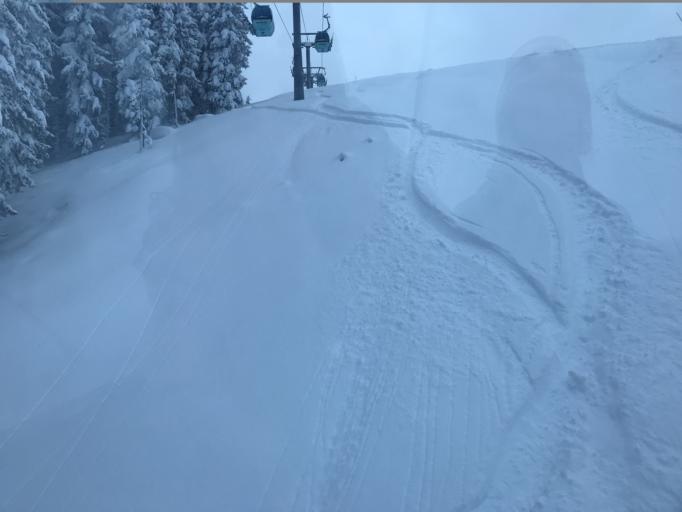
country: AT
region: Salzburg
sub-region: Politischer Bezirk Zell am See
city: Kaprun
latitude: 47.3144
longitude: 12.7522
